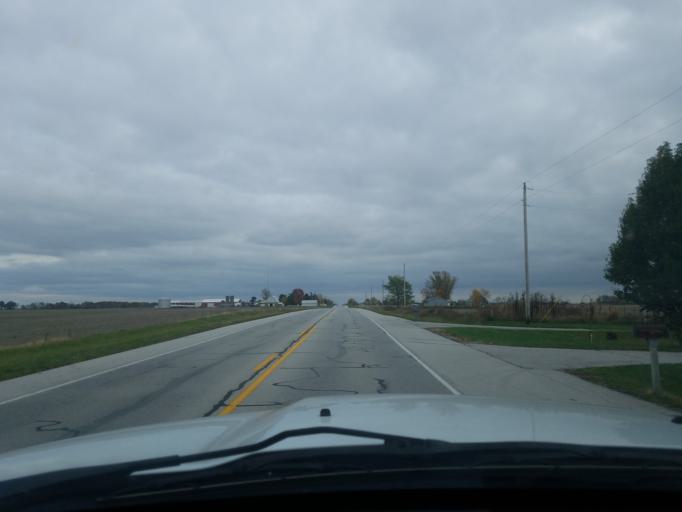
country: US
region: Indiana
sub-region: Johnson County
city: Franklin
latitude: 39.4952
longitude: -85.9317
